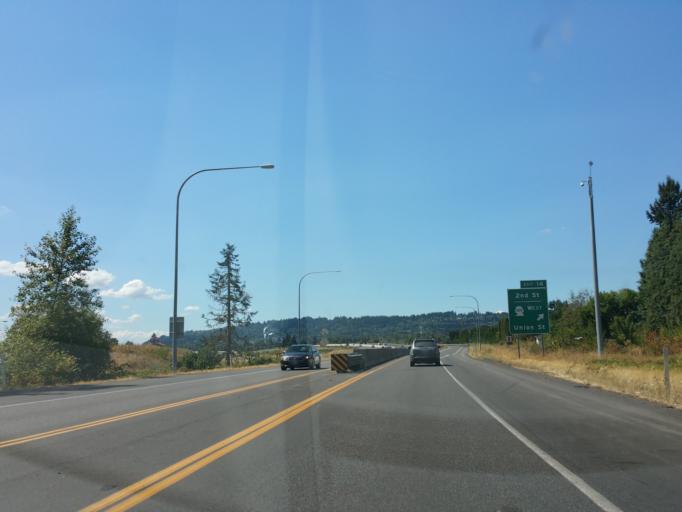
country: US
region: Washington
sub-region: Clark County
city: Washougal
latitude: 45.5791
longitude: -122.3688
